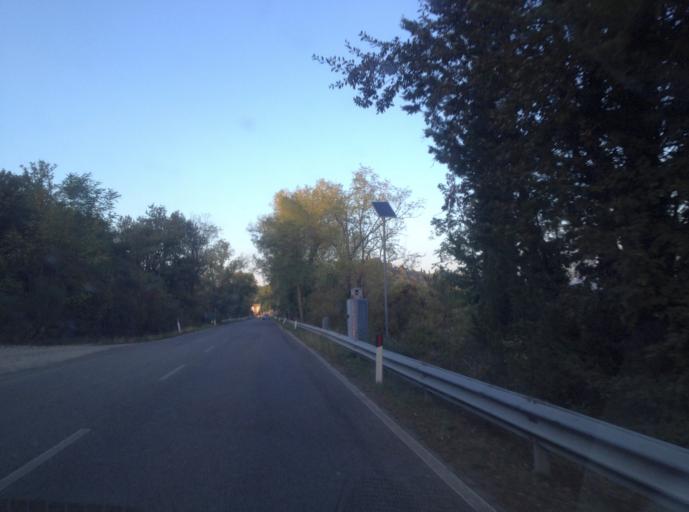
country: IT
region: Tuscany
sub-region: Provincia di Siena
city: Castellina in Chianti
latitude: 43.4877
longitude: 11.2994
